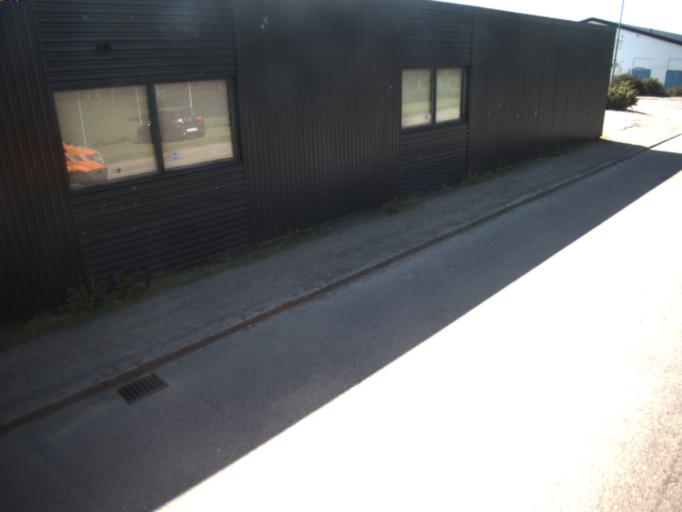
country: SE
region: Skane
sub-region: Helsingborg
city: Helsingborg
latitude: 56.0667
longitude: 12.7094
